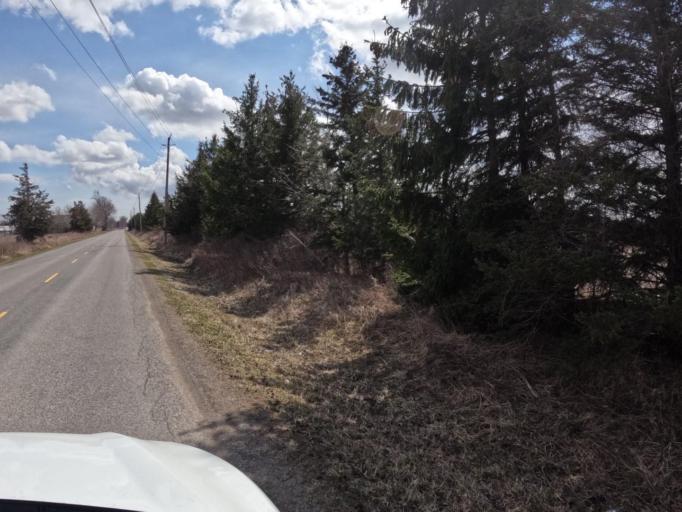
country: CA
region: Ontario
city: Brantford
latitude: 42.9785
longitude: -80.2193
